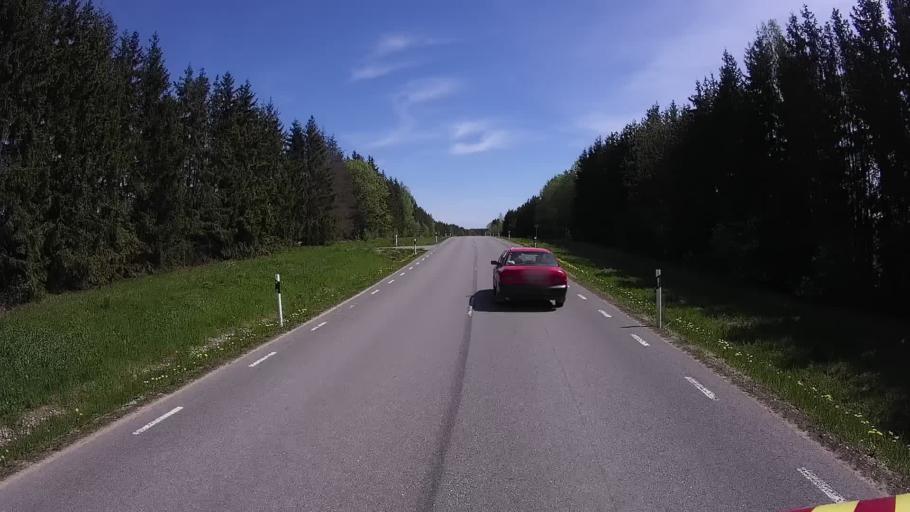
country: LV
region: Apes Novads
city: Ape
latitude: 57.5946
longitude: 26.6249
